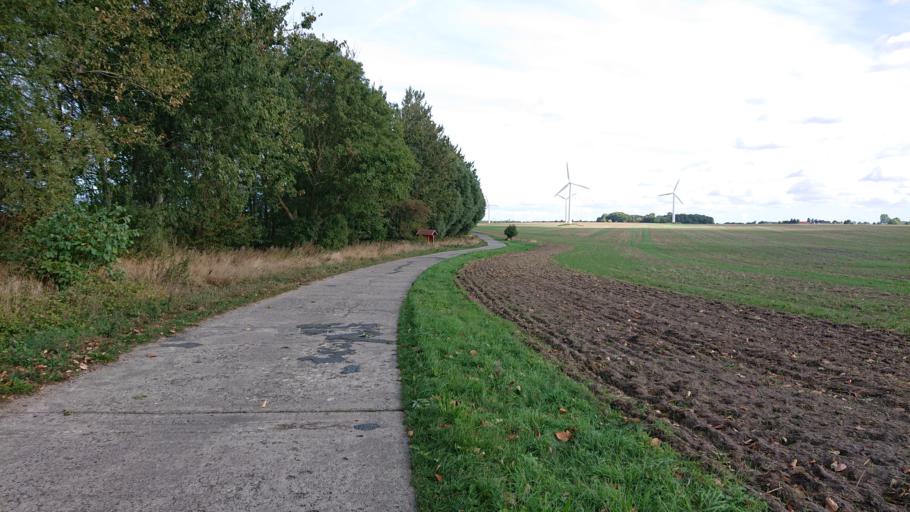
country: DE
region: Mecklenburg-Vorpommern
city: Altefahr
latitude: 54.3378
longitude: 13.1310
